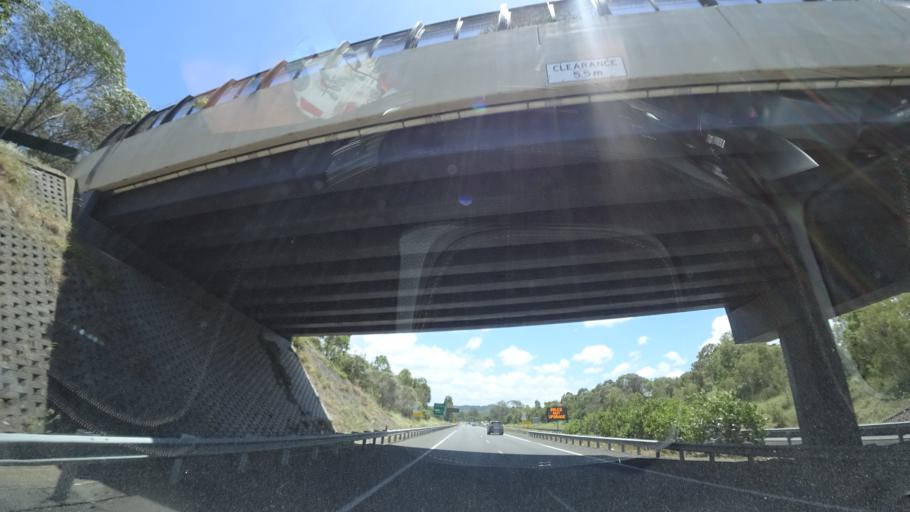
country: AU
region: Queensland
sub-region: Sunshine Coast
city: Little Mountain
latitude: -26.7766
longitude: 153.0578
